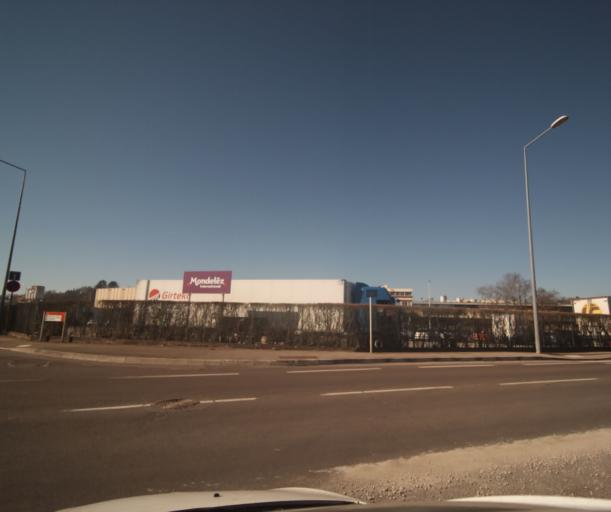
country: FR
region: Franche-Comte
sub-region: Departement du Doubs
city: Pirey
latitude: 47.2412
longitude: 5.9864
